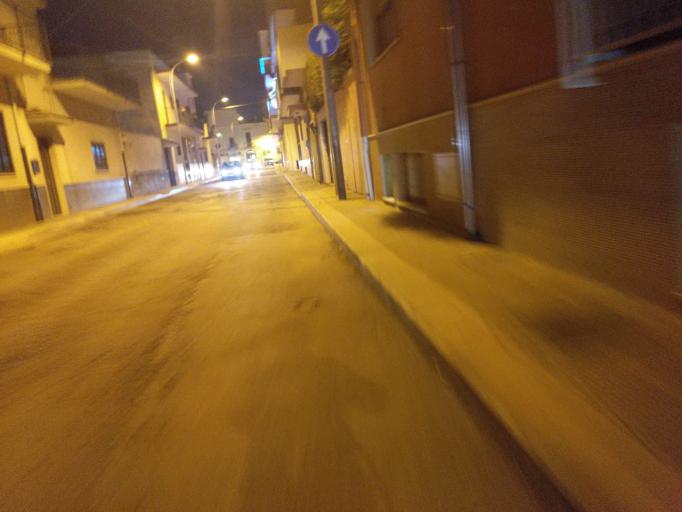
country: IT
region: Apulia
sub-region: Provincia di Bari
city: Modugno
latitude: 41.0806
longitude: 16.7844
